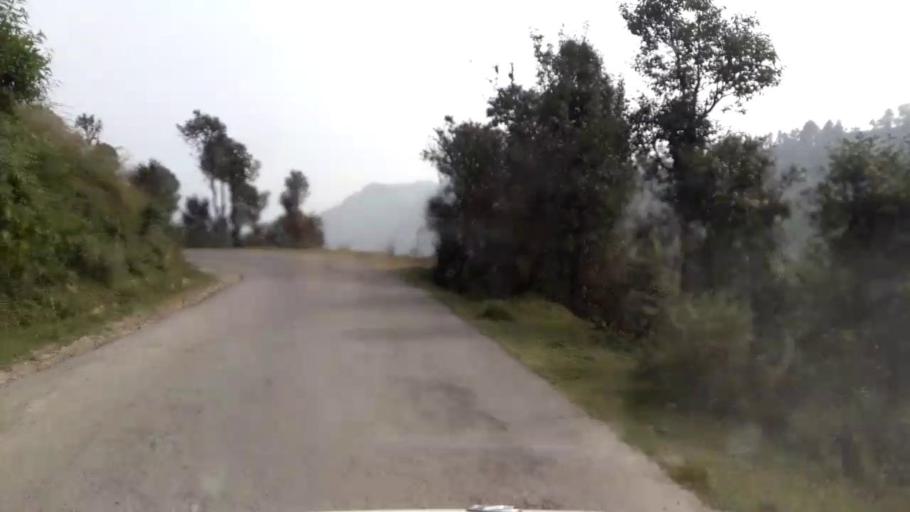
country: IN
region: Himachal Pradesh
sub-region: Shimla
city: Shimla
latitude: 31.0522
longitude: 77.1520
